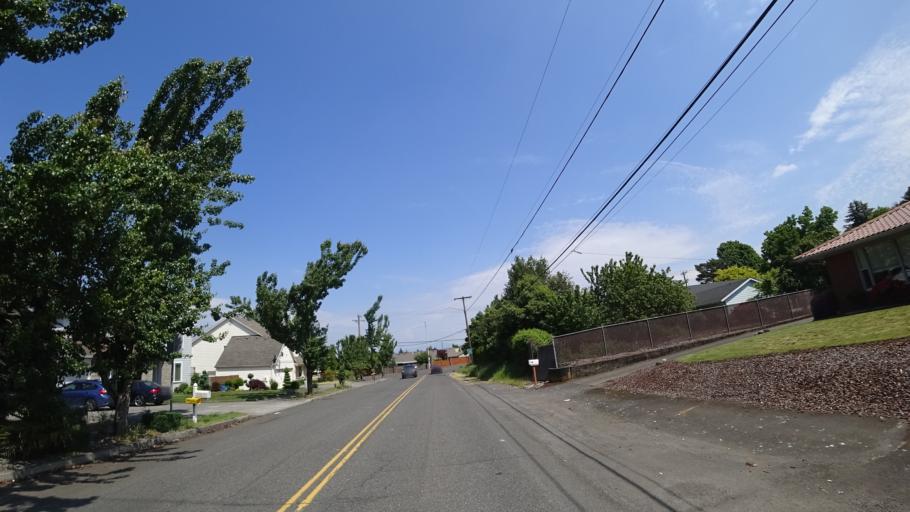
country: US
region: Oregon
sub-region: Multnomah County
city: Fairview
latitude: 45.5379
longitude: -122.5114
